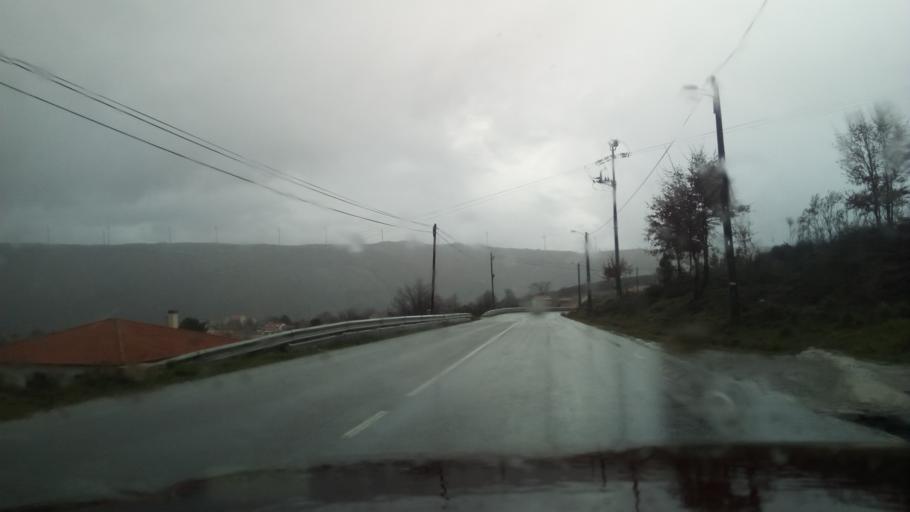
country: PT
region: Guarda
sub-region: Guarda
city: Guarda
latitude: 40.5414
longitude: -7.3158
